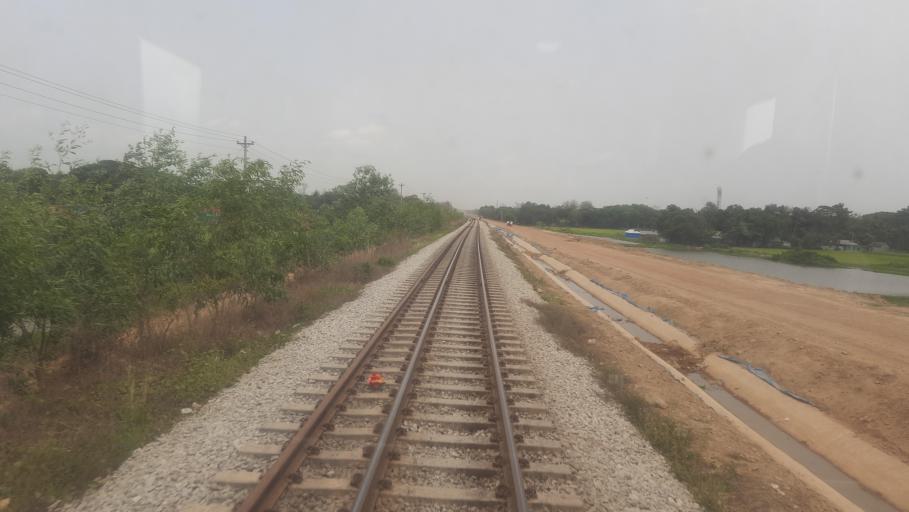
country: BD
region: Chittagong
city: Comilla
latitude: 23.4879
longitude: 91.1628
